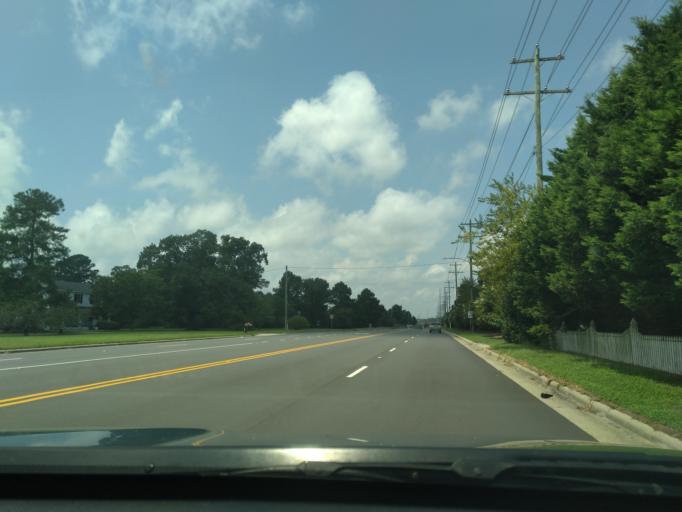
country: US
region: North Carolina
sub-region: Nash County
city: Rocky Mount
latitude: 35.9889
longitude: -77.8197
